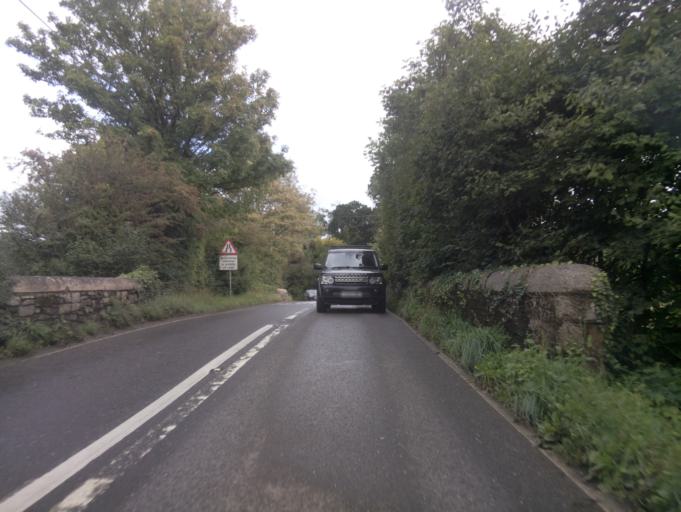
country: GB
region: England
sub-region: Devon
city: Modbury
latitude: 50.3513
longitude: -3.9256
